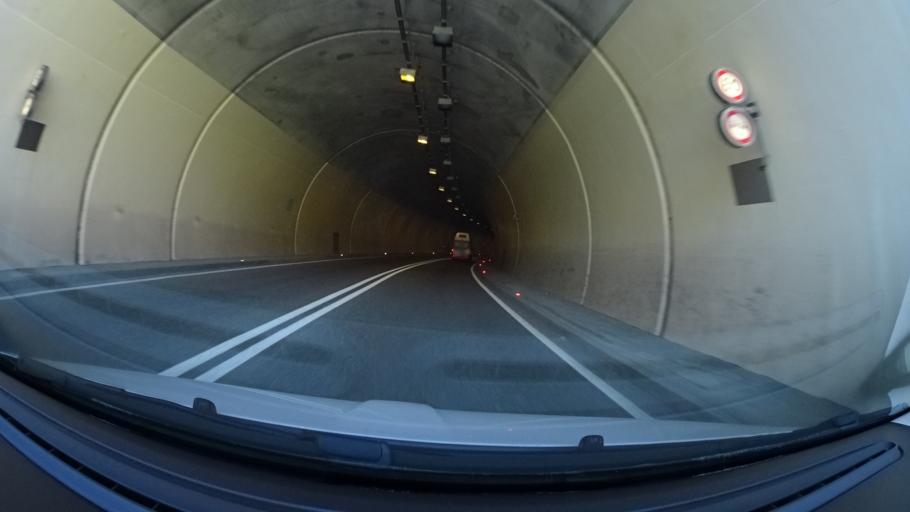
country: IT
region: Trentino-Alto Adige
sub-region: Bolzano
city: Santa Cristina Valgardena
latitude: 46.5566
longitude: 11.7315
